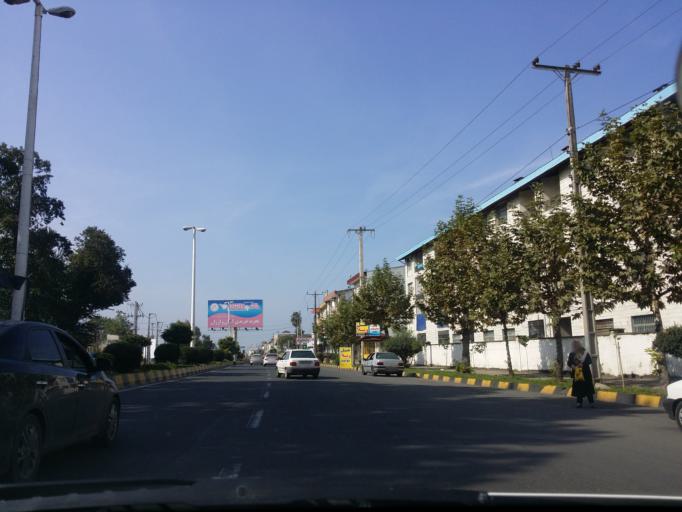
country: IR
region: Mazandaran
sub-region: Nowshahr
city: Nowshahr
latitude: 36.6565
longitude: 51.4870
